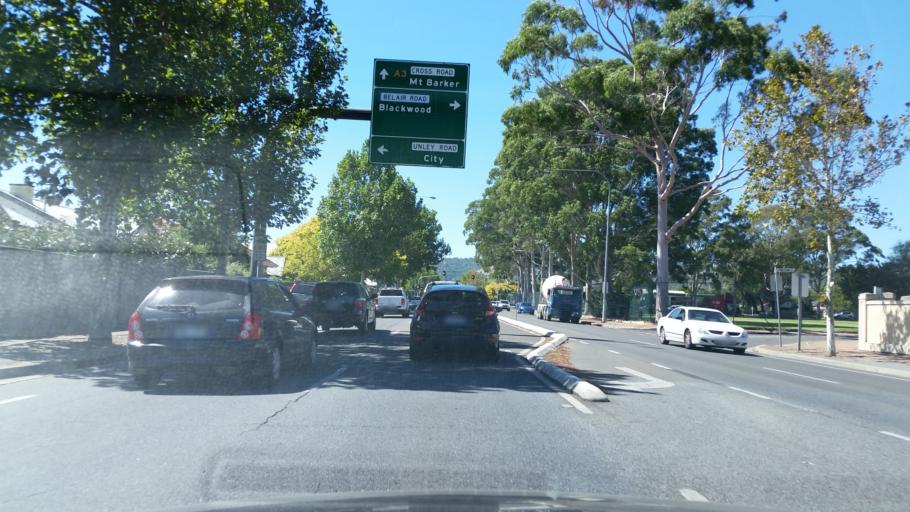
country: AU
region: South Australia
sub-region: Unley
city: Unley Park
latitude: -34.9655
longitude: 138.6066
